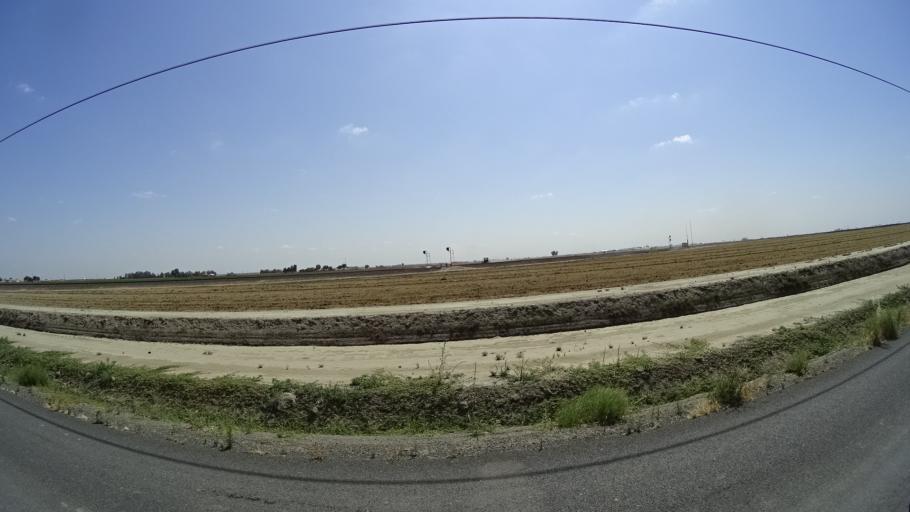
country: US
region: California
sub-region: Kings County
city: Home Garden
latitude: 36.2057
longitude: -119.6371
